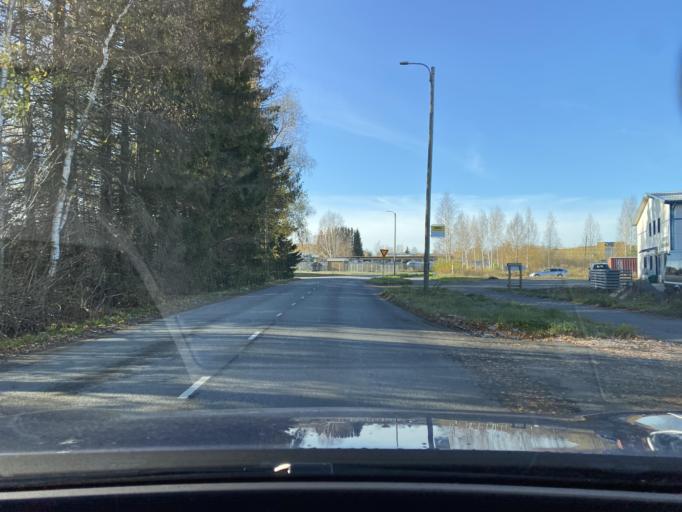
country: FI
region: Haeme
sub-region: Haemeenlinna
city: Haemeenlinna
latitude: 61.0146
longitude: 24.4086
